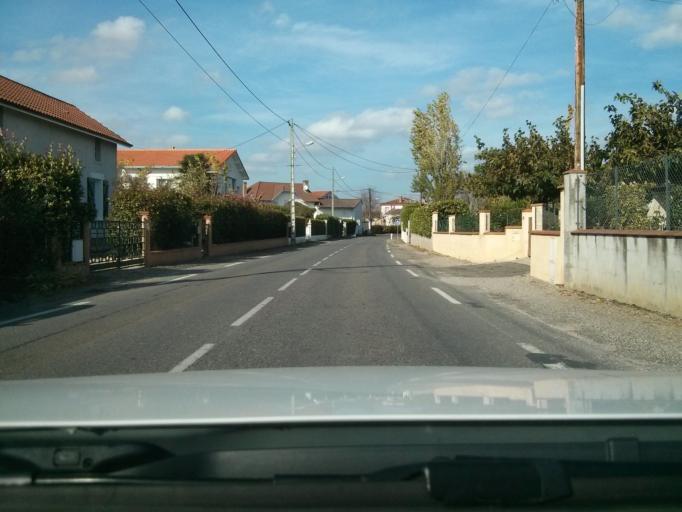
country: FR
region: Midi-Pyrenees
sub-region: Departement du Tarn-et-Garonne
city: Montbeton
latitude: 44.0138
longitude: 1.3221
